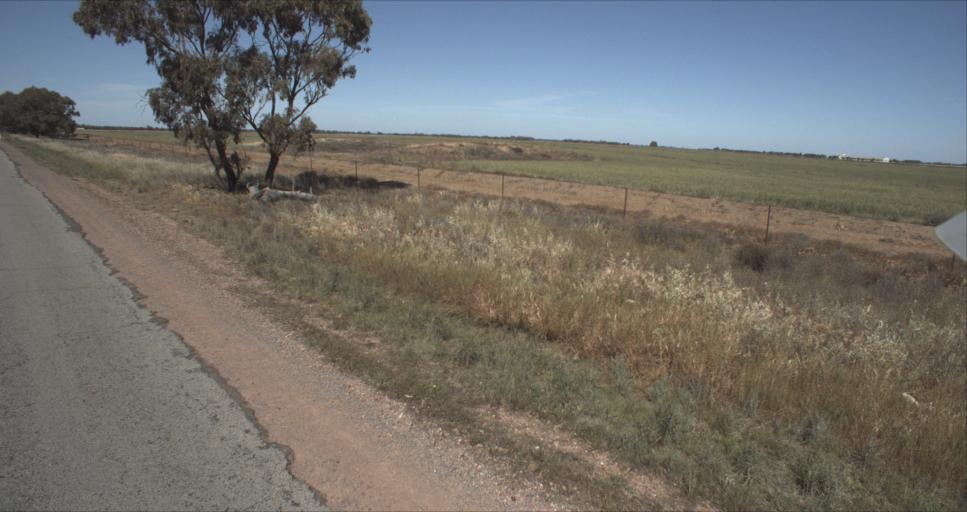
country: AU
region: New South Wales
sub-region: Leeton
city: Leeton
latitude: -34.5543
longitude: 146.3140
